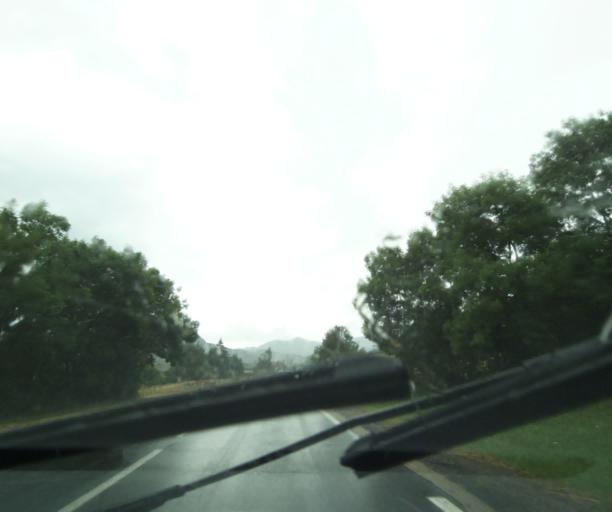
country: FR
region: Auvergne
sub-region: Departement de la Haute-Loire
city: Saint-Julien-Chapteuil
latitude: 45.0692
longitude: 4.0416
